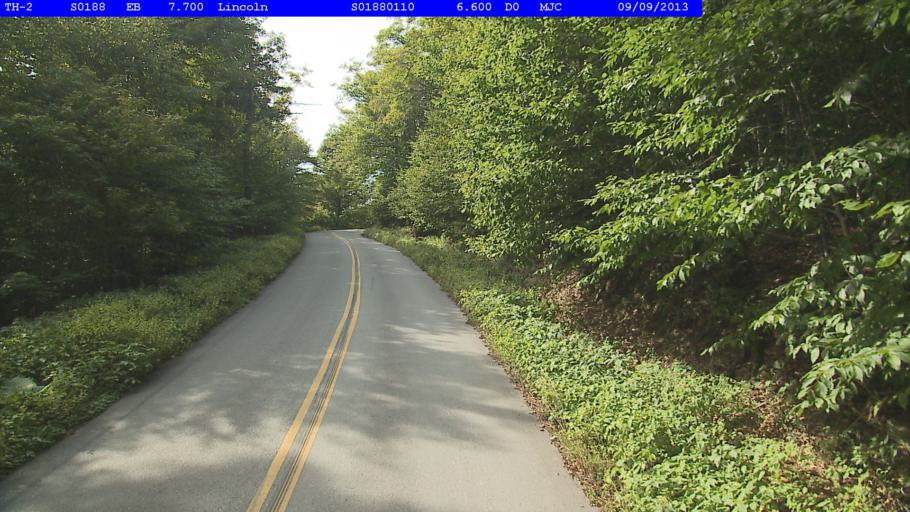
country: US
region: Vermont
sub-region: Addison County
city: Bristol
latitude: 44.0939
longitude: -72.9318
